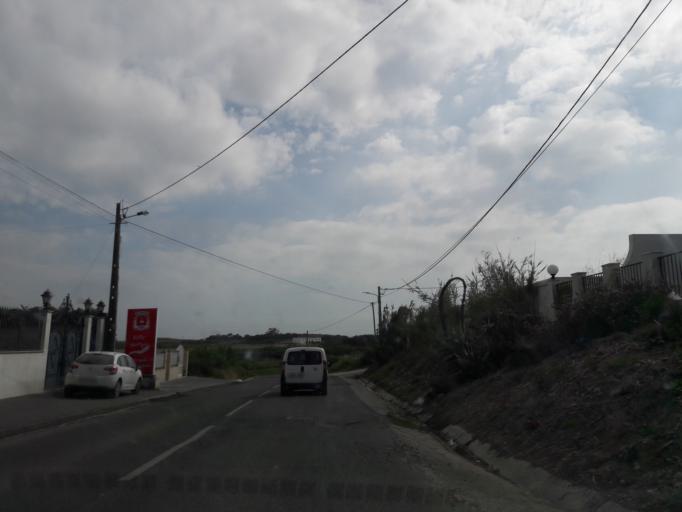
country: PT
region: Leiria
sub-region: Peniche
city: Atouguia da Baleia
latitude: 39.3607
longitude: -9.3183
